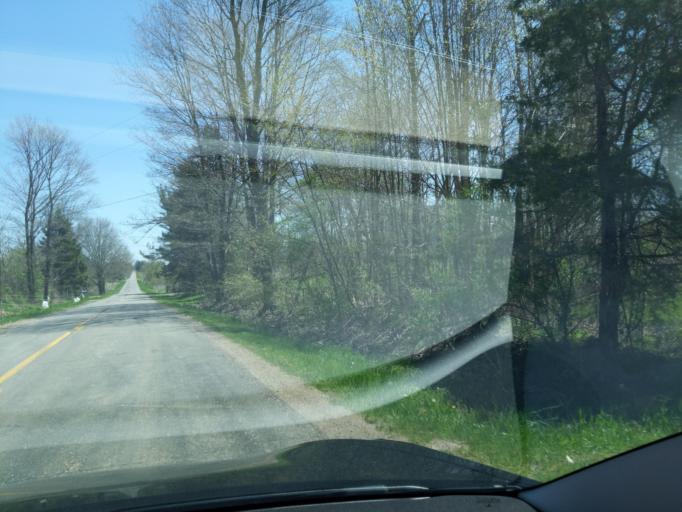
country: US
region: Michigan
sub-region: Ingham County
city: Holt
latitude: 42.5530
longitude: -84.5573
